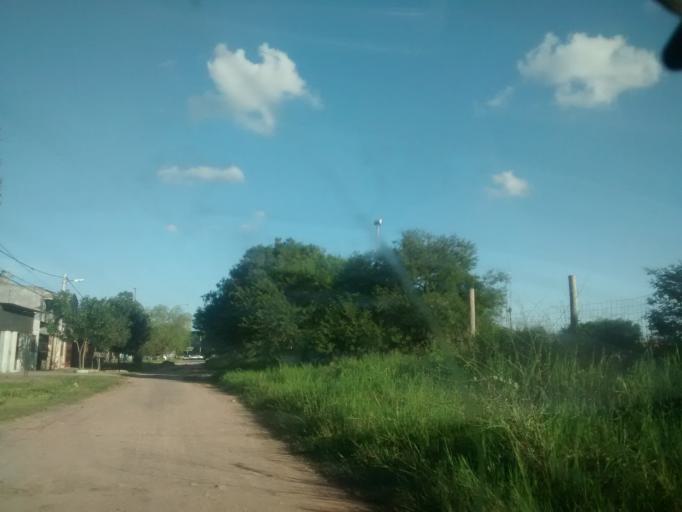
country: AR
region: Chaco
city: Fontana
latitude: -27.4522
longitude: -59.0194
